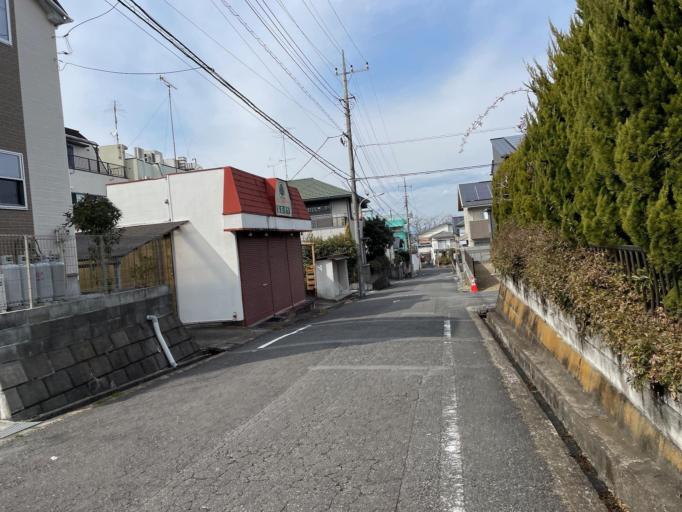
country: JP
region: Tokyo
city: Hachioji
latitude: 35.6364
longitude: 139.3627
